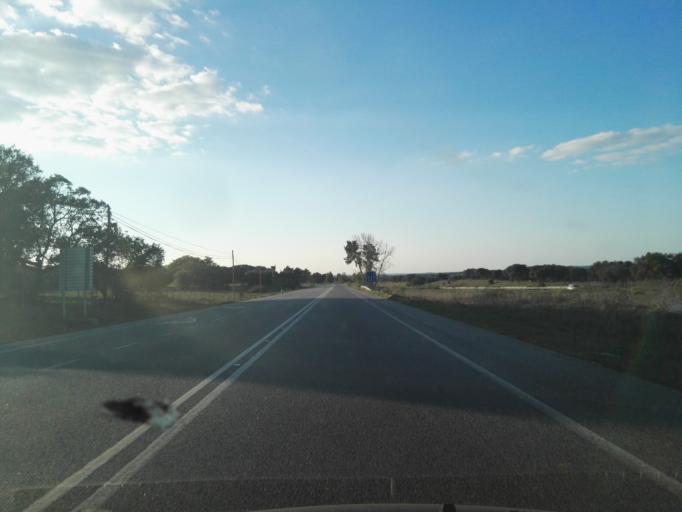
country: PT
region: Evora
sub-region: Arraiolos
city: Arraiolos
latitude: 38.6090
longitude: -8.0607
